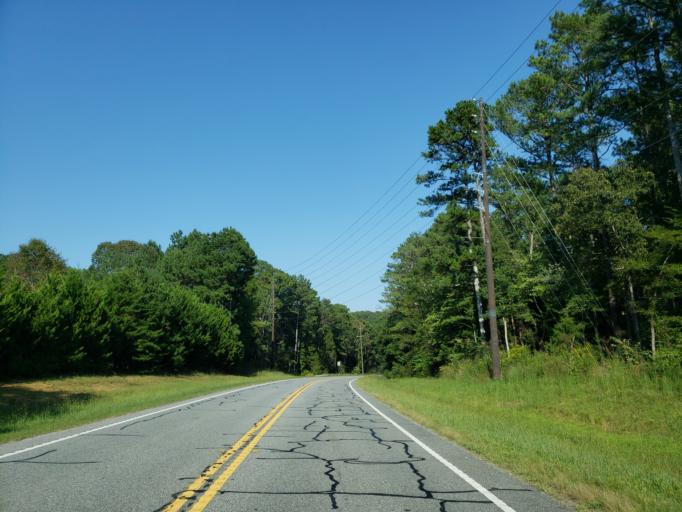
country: US
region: Georgia
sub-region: Whitfield County
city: Varnell
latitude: 34.9019
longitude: -85.0231
